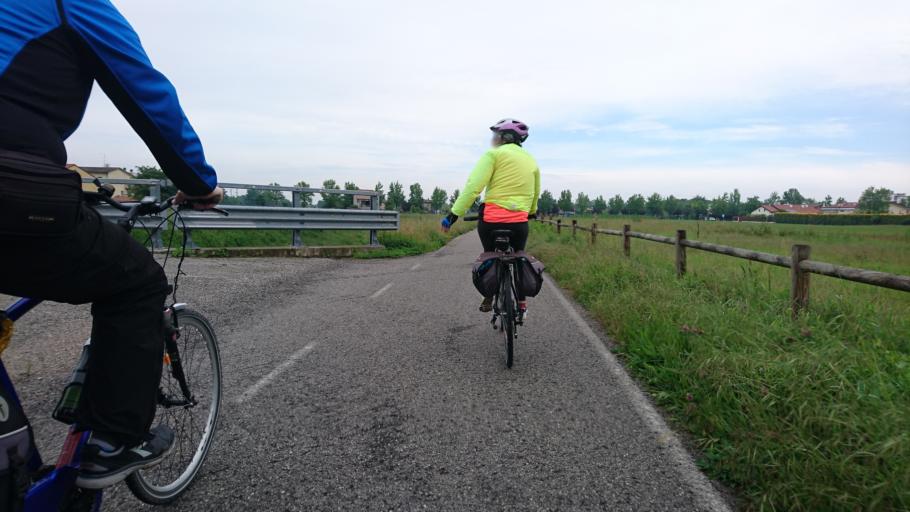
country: IT
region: Veneto
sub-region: Provincia di Padova
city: Montegrotto Terme
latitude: 45.3305
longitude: 11.7757
